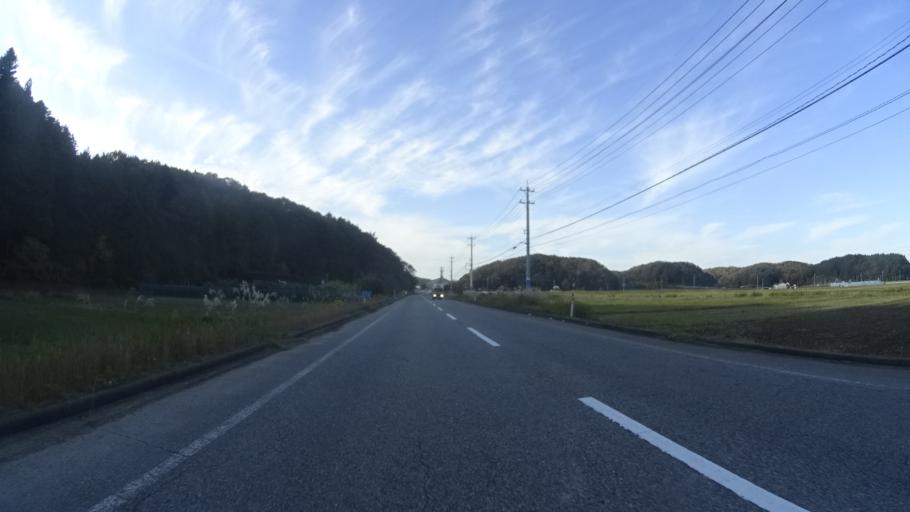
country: JP
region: Ishikawa
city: Hakui
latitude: 37.0178
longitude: 136.7929
